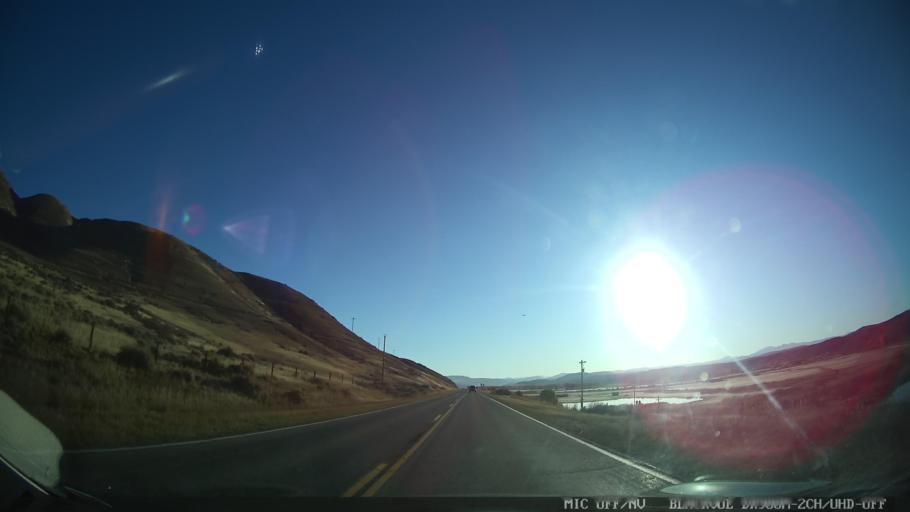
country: US
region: Colorado
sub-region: Grand County
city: Kremmling
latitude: 40.0521
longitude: -106.3431
